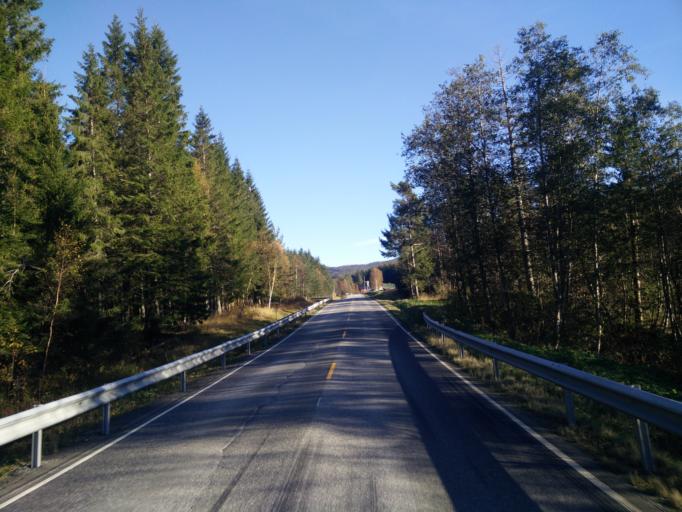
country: NO
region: More og Romsdal
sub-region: Halsa
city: Liaboen
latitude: 63.0720
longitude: 8.2766
